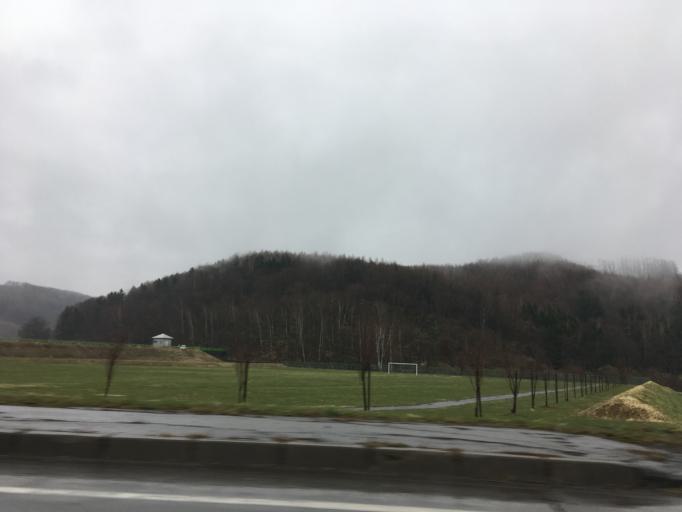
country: JP
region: Hokkaido
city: Nayoro
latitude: 44.0935
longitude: 142.4244
